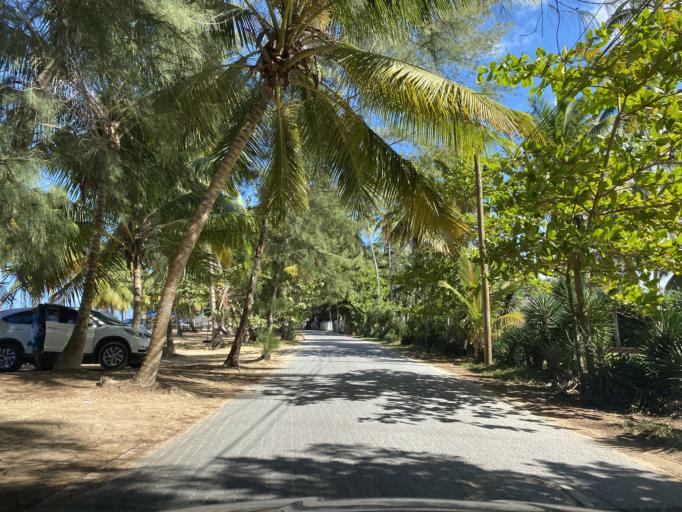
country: DO
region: Samana
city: Las Terrenas
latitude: 19.3256
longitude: -69.5495
